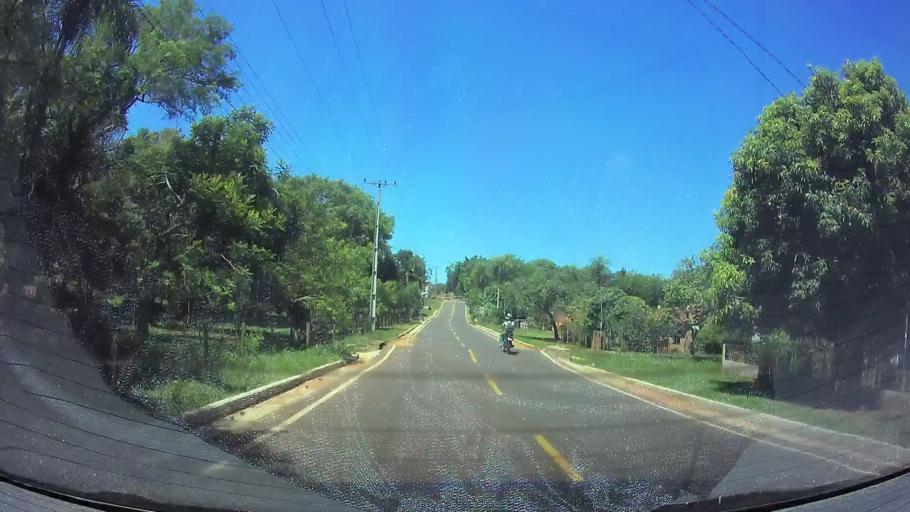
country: PY
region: Central
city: Aregua
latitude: -25.2568
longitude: -57.4473
